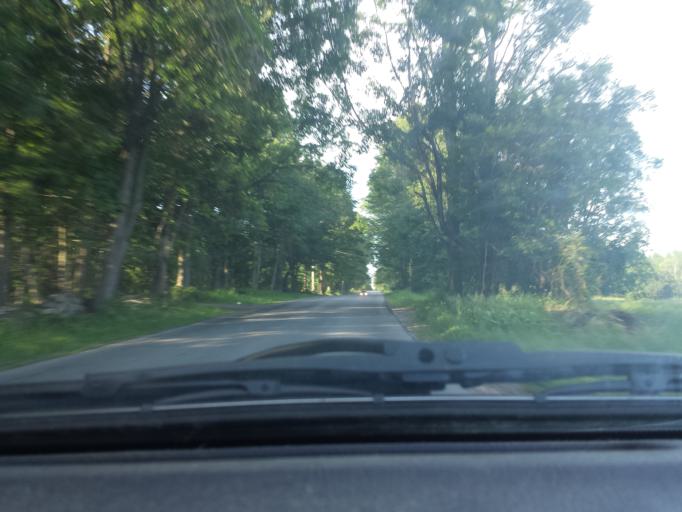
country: US
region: New York
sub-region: St. Lawrence County
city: Potsdam
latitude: 44.7011
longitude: -74.9656
